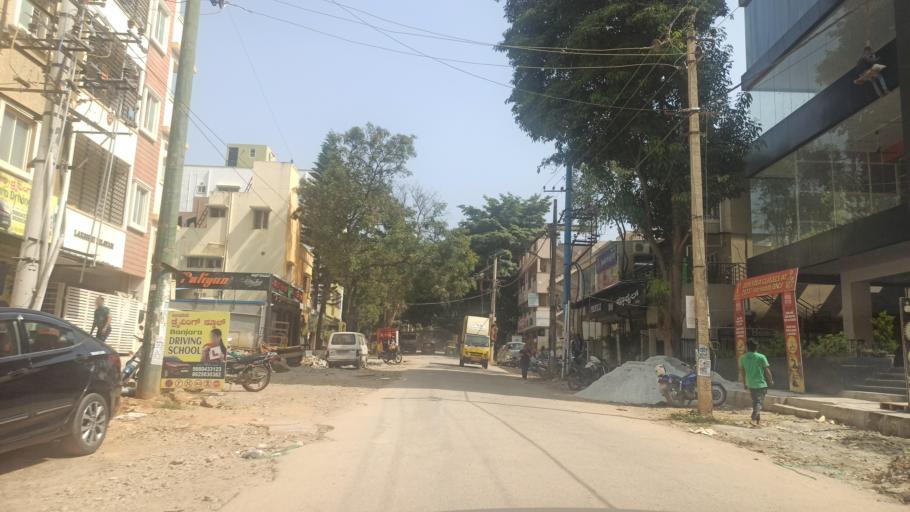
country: IN
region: Karnataka
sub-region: Bangalore Urban
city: Bangalore
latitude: 12.9635
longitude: 77.7094
